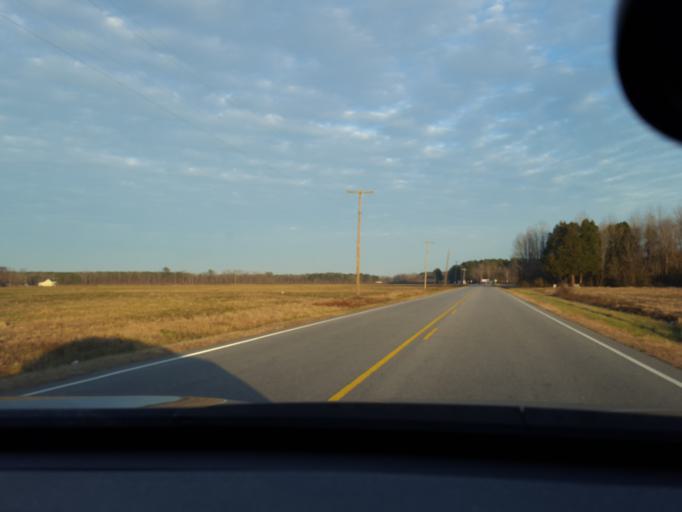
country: US
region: North Carolina
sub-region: Hertford County
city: Murfreesboro
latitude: 36.2882
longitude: -77.1851
